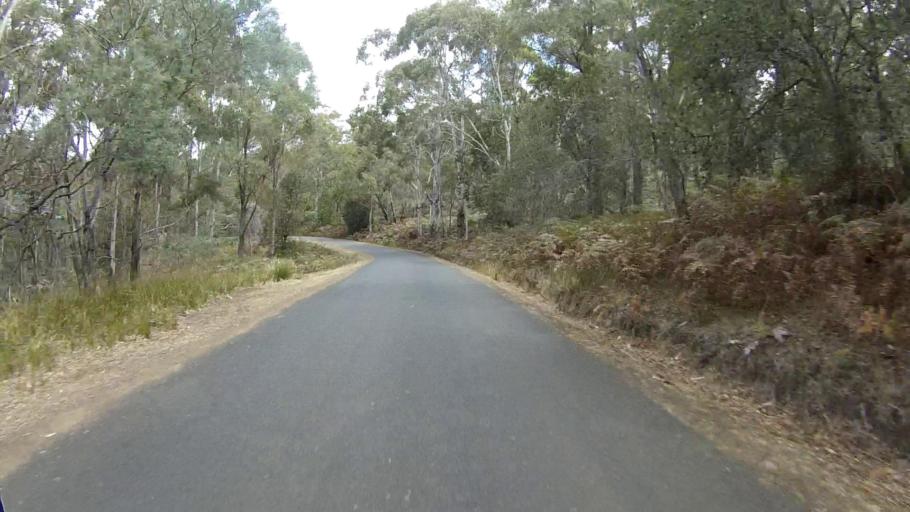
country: AU
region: Tasmania
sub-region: Sorell
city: Sorell
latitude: -42.6025
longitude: 147.9220
